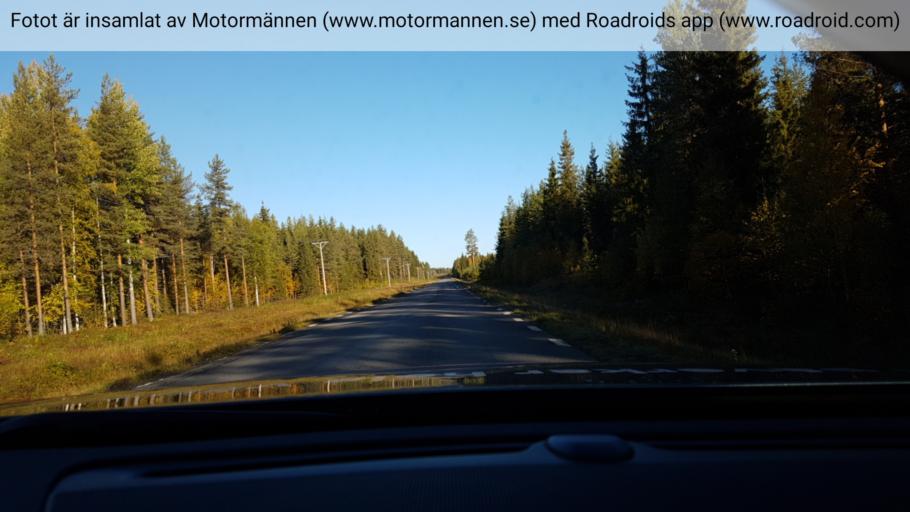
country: SE
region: Norrbotten
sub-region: Bodens Kommun
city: Boden
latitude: 65.9353
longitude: 21.6456
